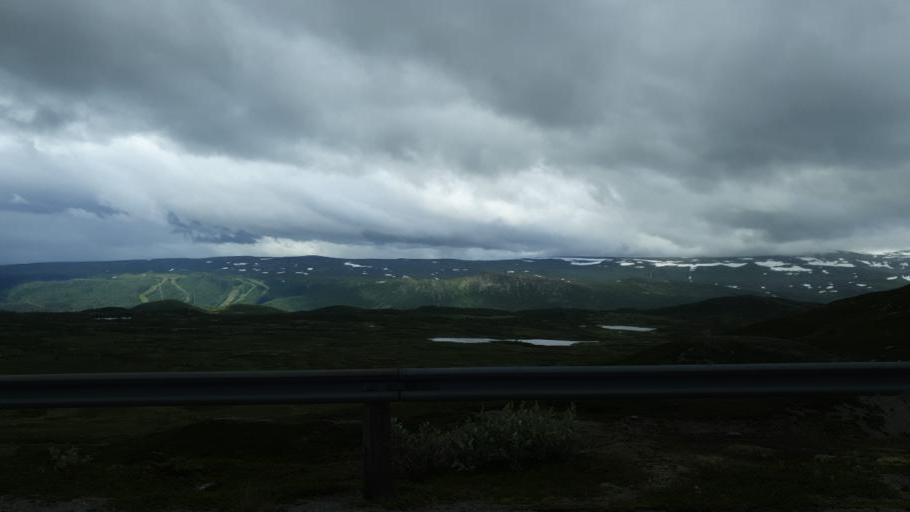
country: NO
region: Oppland
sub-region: Vestre Slidre
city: Slidre
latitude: 61.2807
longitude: 8.8409
